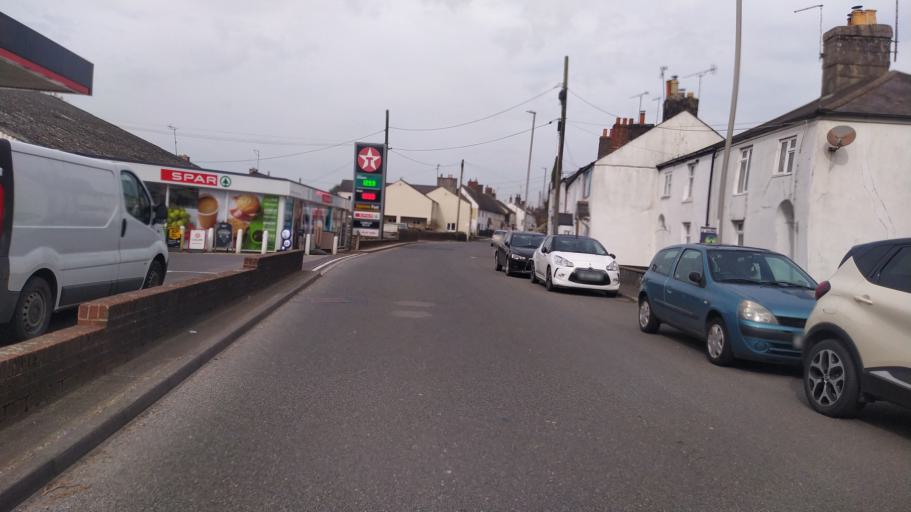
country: GB
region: England
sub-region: Dorset
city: Dorchester
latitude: 50.7764
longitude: -2.5696
